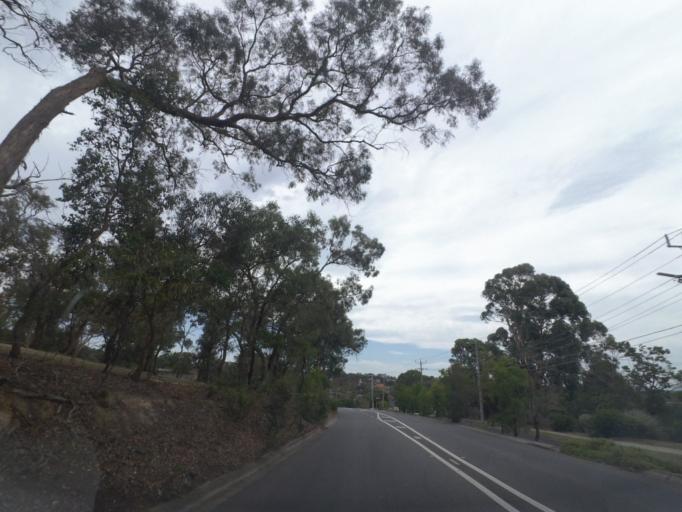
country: AU
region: Victoria
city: Saint Helena
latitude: -37.6922
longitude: 145.1294
